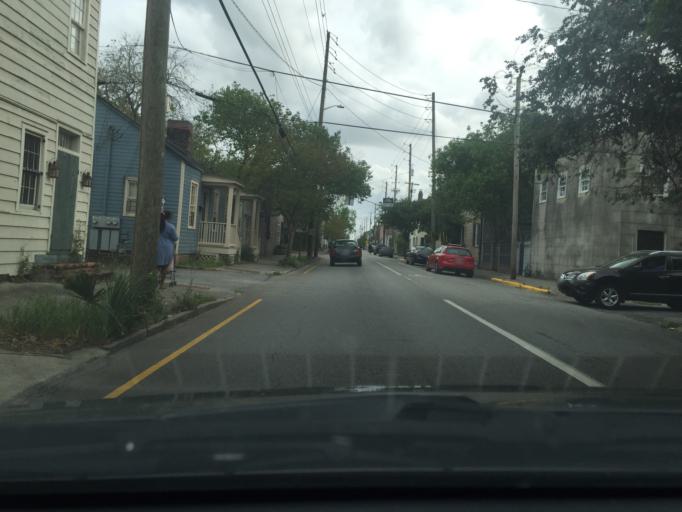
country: US
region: Georgia
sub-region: Chatham County
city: Savannah
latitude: 32.0717
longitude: -81.0889
